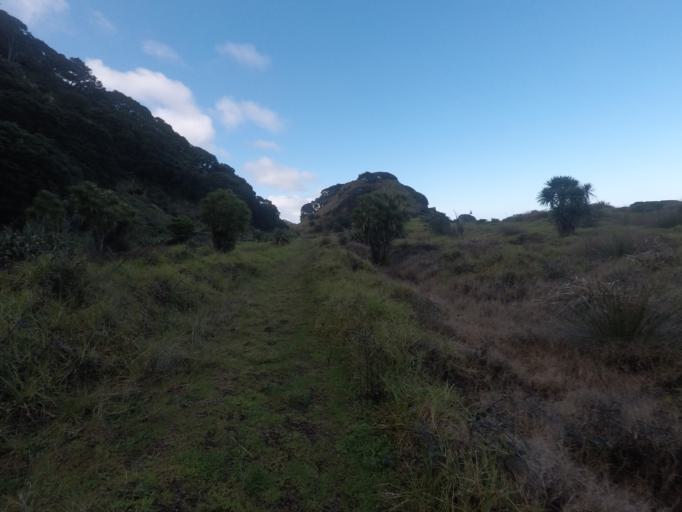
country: NZ
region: Auckland
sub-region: Auckland
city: Titirangi
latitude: -37.0013
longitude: 174.4802
